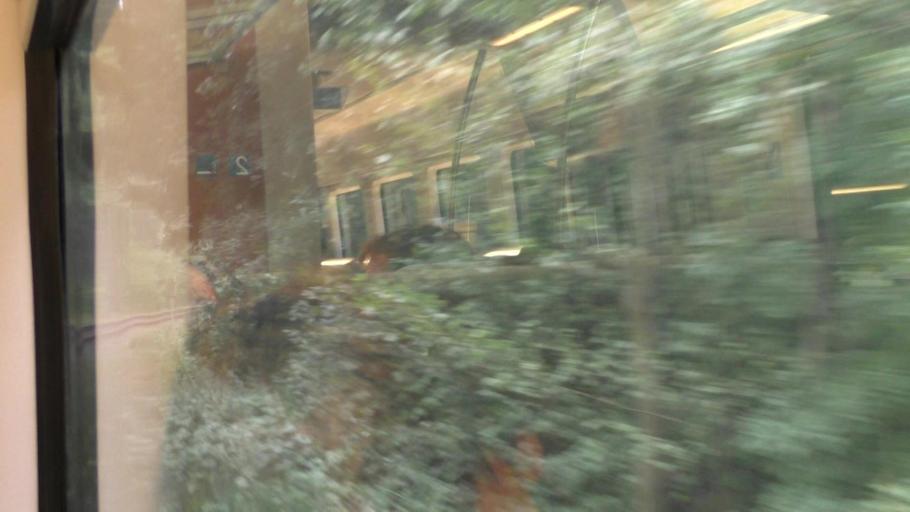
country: DE
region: Saxony
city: Eibau
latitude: 50.9692
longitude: 14.6739
